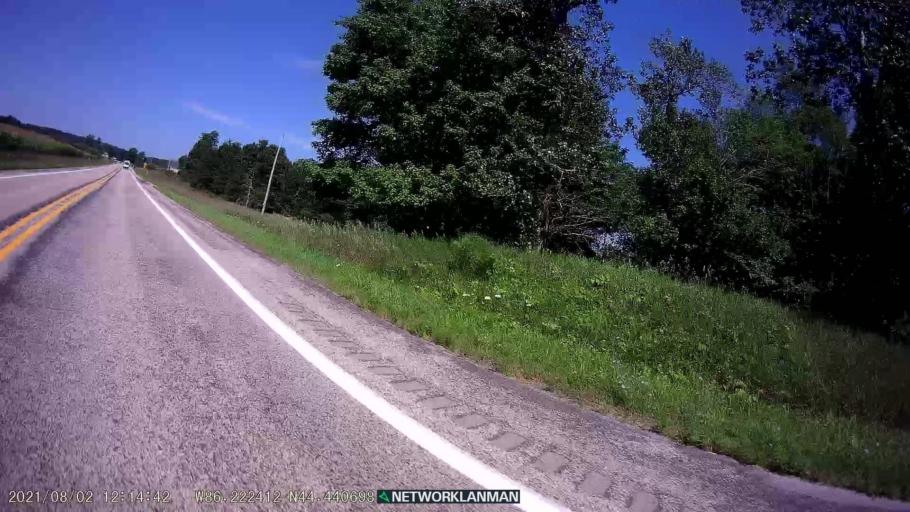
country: US
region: Michigan
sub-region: Benzie County
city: Frankfort
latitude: 44.4409
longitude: -86.2223
